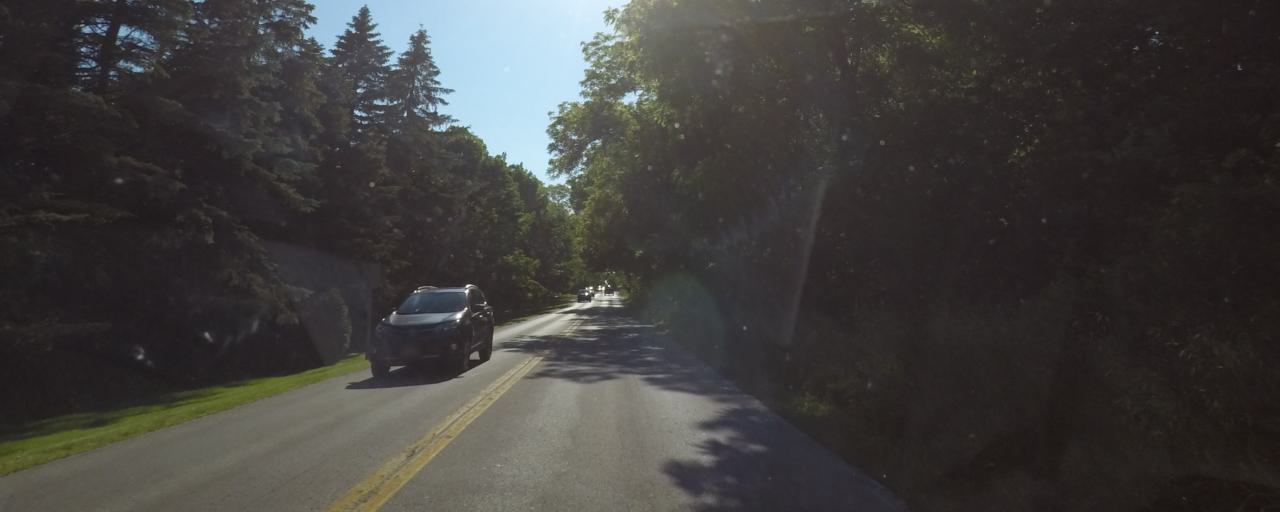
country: US
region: Wisconsin
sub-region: Milwaukee County
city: Greenfield
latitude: 42.9448
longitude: -88.0268
